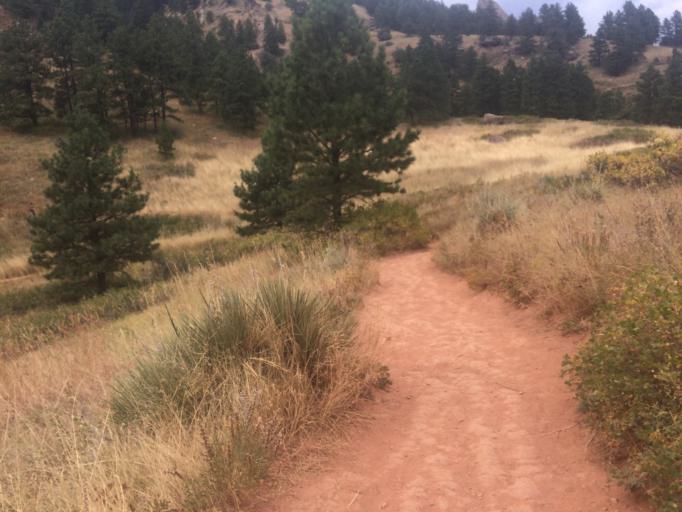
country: US
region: Colorado
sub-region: Boulder County
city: Boulder
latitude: 39.9778
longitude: -105.2838
